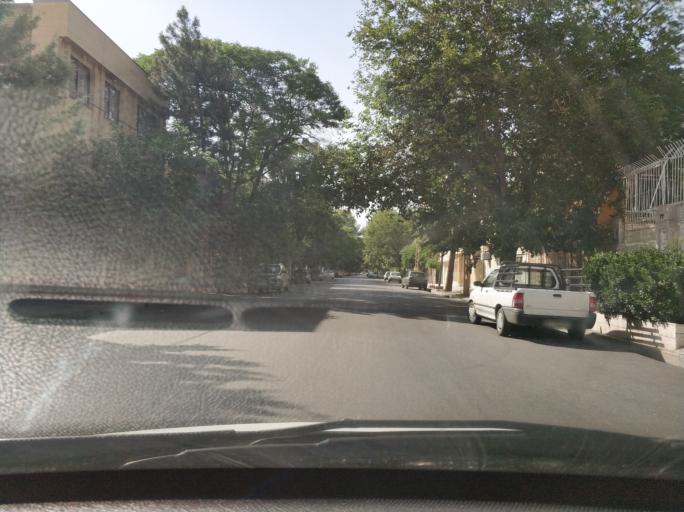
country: IR
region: Razavi Khorasan
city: Mashhad
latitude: 36.2712
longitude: 59.5986
